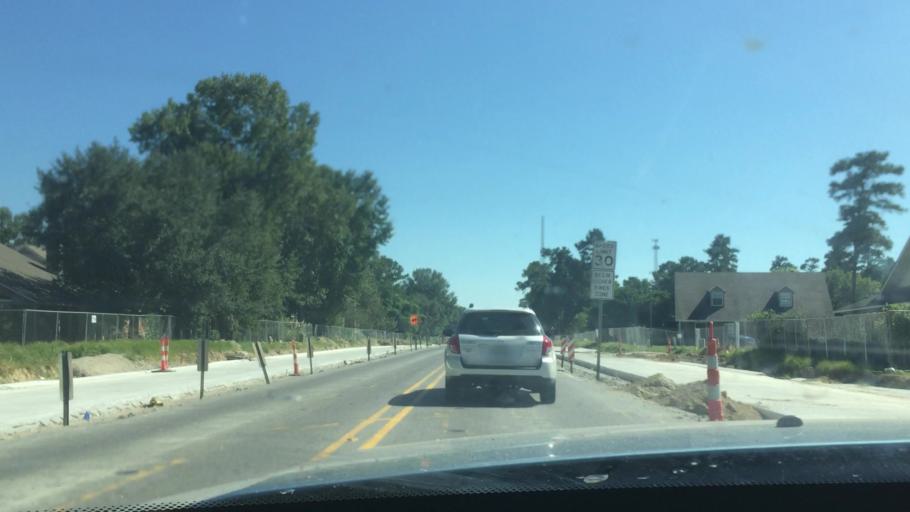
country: US
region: Louisiana
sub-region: East Baton Rouge Parish
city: Shenandoah
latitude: 30.4240
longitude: -91.0075
